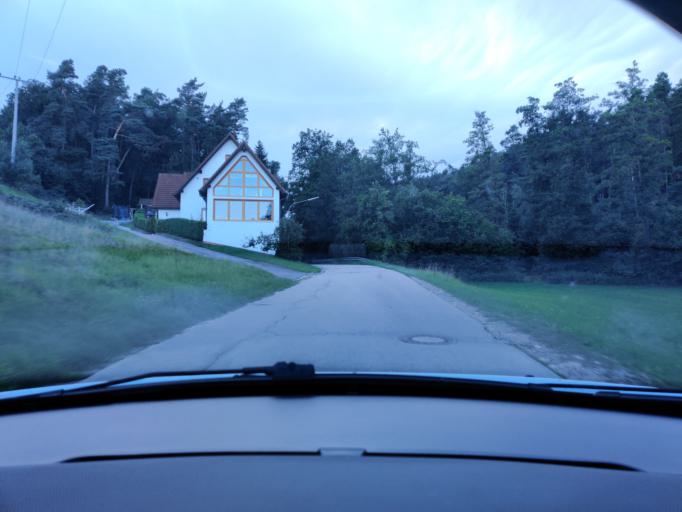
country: DE
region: Bavaria
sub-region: Upper Palatinate
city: Pfreimd
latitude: 49.4862
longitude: 12.1619
